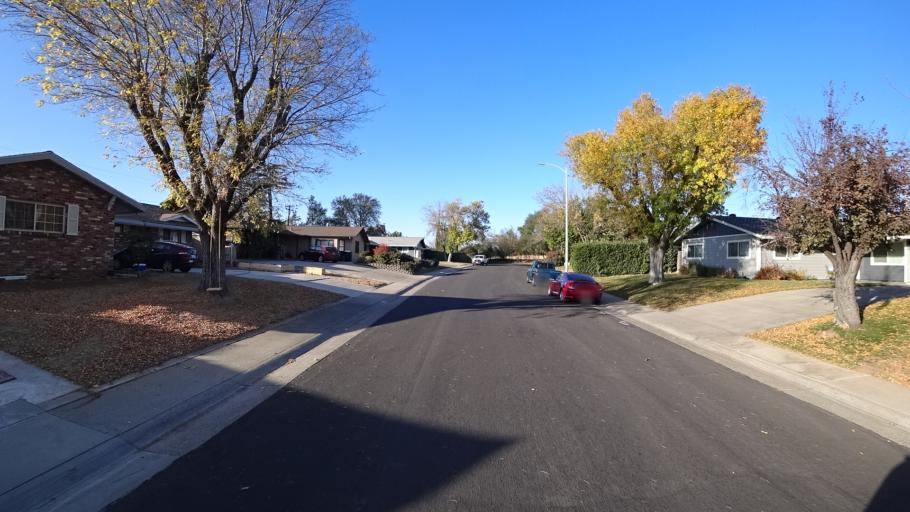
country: US
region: California
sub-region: Sacramento County
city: Citrus Heights
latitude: 38.6989
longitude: -121.2942
